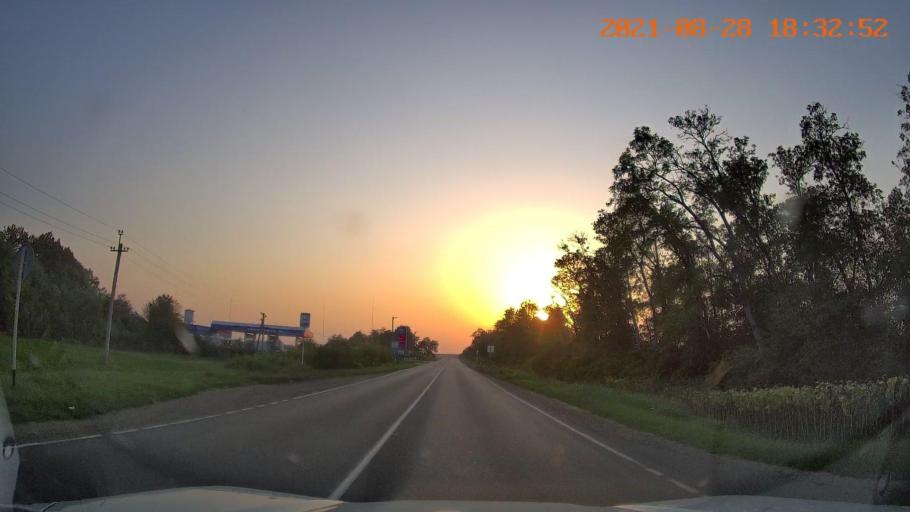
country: RU
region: Adygeya
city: Giaginskaya
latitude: 44.8773
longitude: 40.1875
